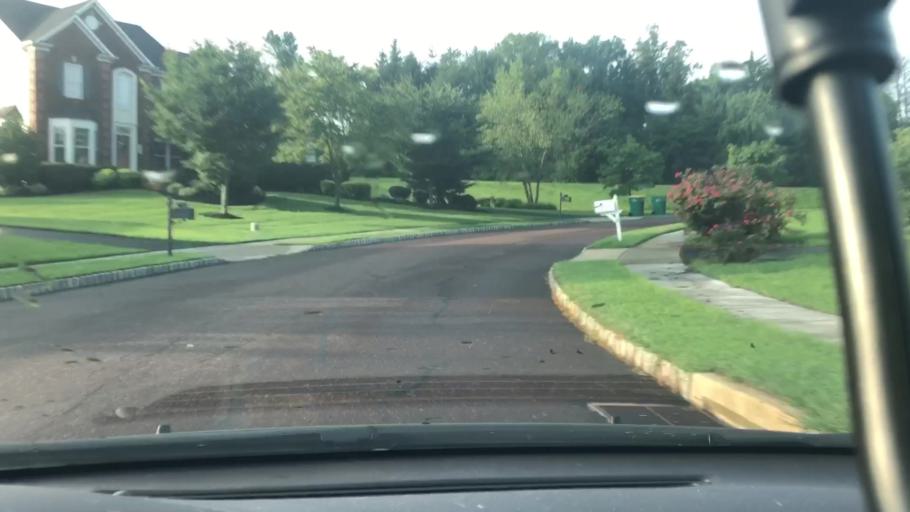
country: US
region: Pennsylvania
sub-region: Chester County
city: Kenilworth
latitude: 40.2143
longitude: -75.6187
